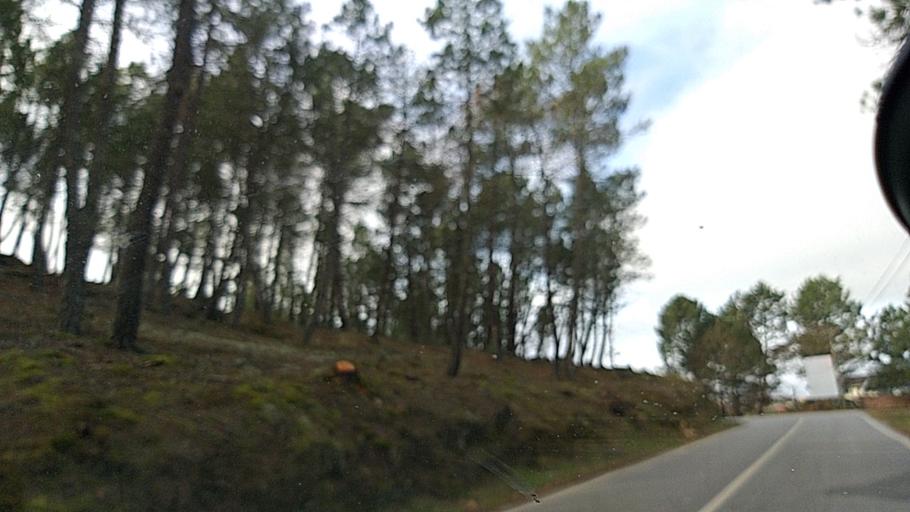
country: PT
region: Guarda
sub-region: Aguiar da Beira
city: Aguiar da Beira
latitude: 40.7683
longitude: -7.5327
